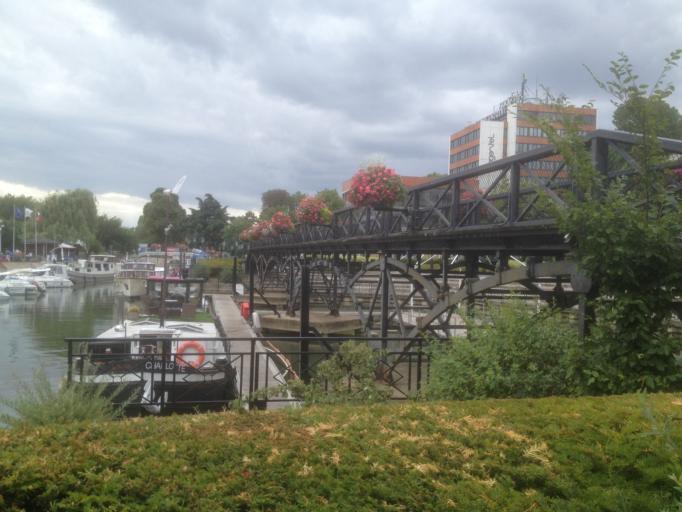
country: FR
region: Ile-de-France
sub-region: Departement du Val-de-Marne
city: Nogent-sur-Marne
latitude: 48.8318
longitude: 2.4917
